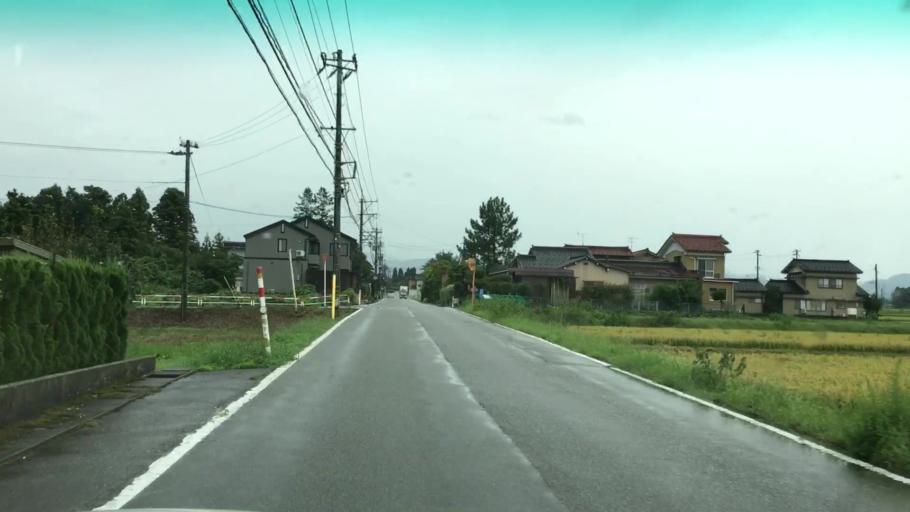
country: JP
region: Toyama
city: Kamiichi
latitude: 36.6460
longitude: 137.3201
